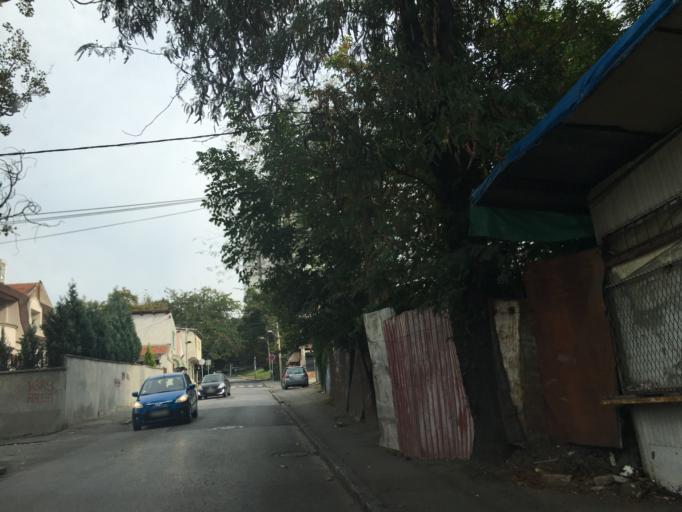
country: RS
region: Central Serbia
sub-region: Belgrade
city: Vracar
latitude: 44.7930
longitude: 20.4898
